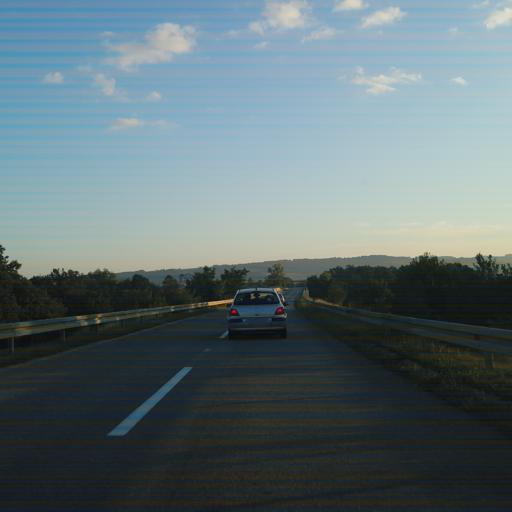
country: RS
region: Central Serbia
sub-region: Zajecarski Okrug
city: Zajecar
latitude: 44.0854
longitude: 22.3392
